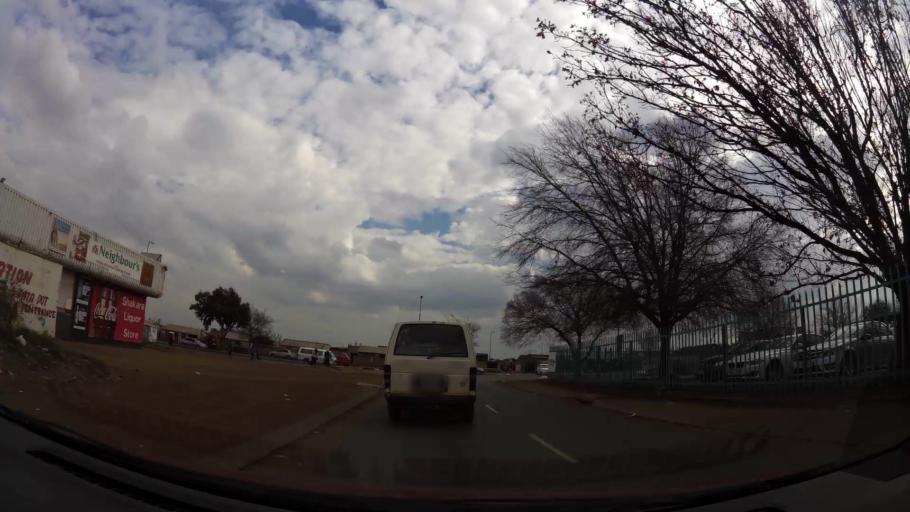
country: ZA
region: Gauteng
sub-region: City of Johannesburg Metropolitan Municipality
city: Soweto
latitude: -26.2521
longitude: 27.8546
